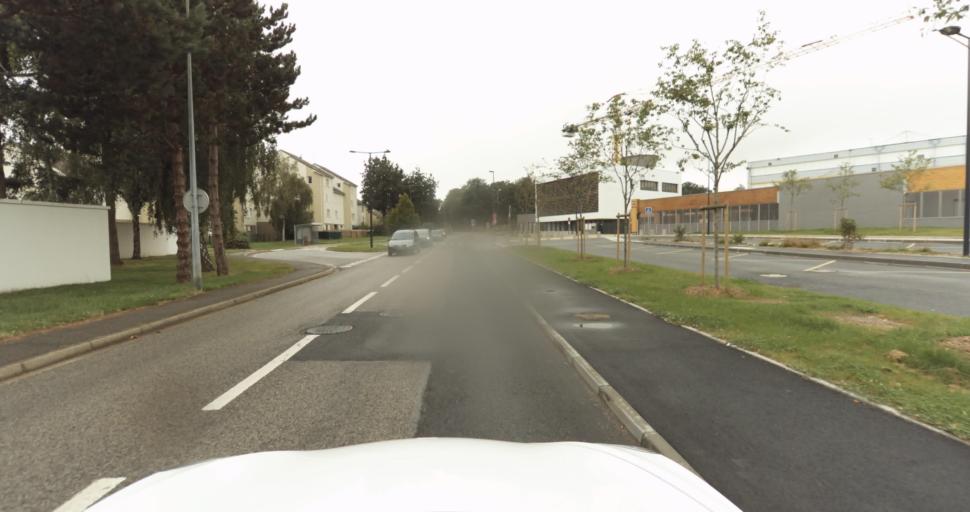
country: FR
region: Haute-Normandie
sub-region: Departement de l'Eure
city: Aviron
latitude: 49.0389
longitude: 1.1304
